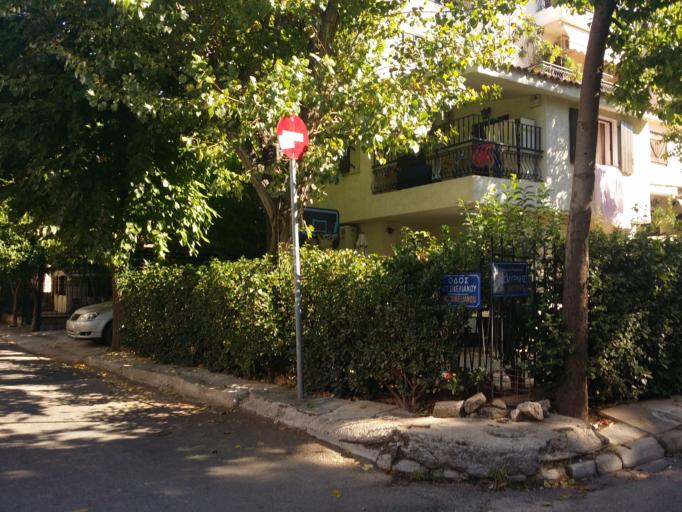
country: GR
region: Attica
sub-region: Nomarchia Athinas
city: Agia Paraskevi
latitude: 38.0177
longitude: 23.8365
